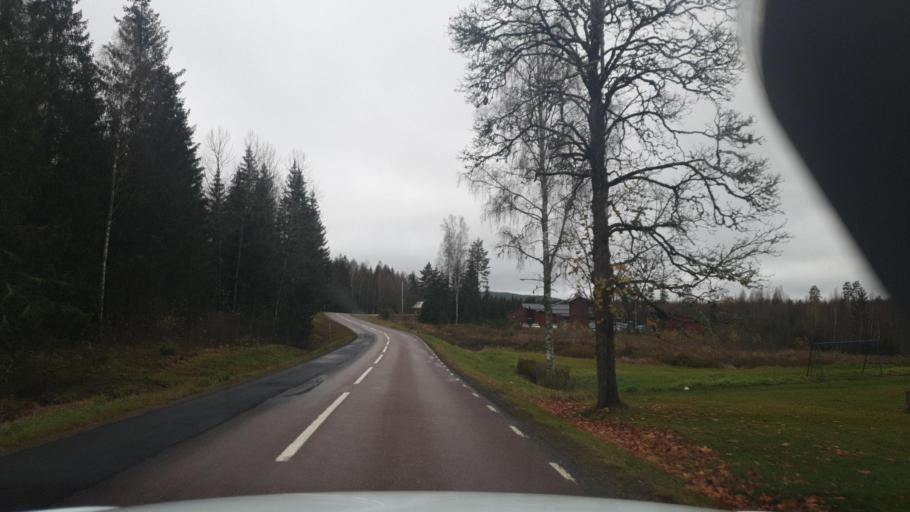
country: SE
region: Vaermland
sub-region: Eda Kommun
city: Amotfors
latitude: 59.7473
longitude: 12.2115
